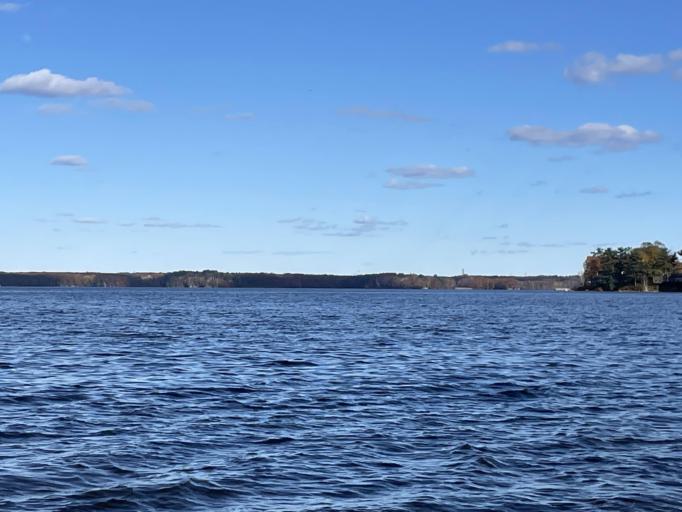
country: US
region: New Hampshire
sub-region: Rockingham County
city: Stratham Station
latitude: 43.0560
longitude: -70.8967
